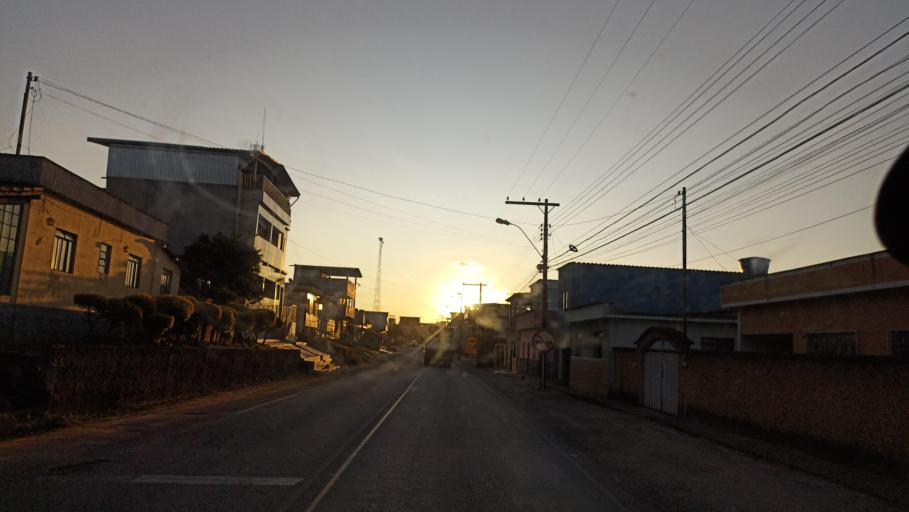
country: BR
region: Minas Gerais
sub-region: Sao Joao Del Rei
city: Sao Joao del Rei
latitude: -21.2435
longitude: -44.4101
